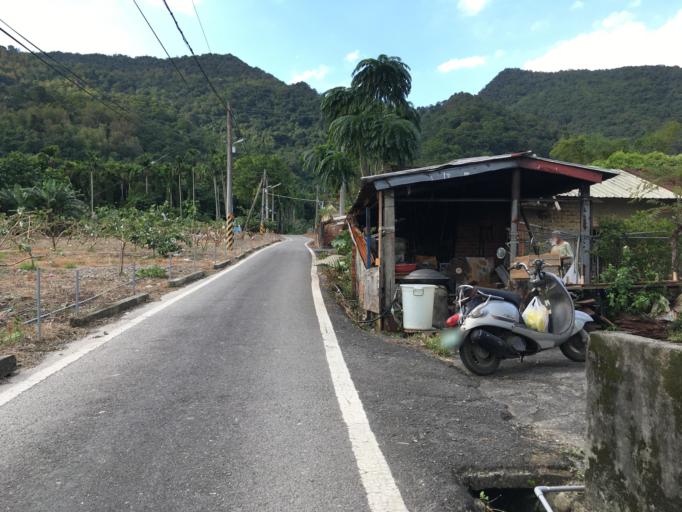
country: TW
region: Taiwan
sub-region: Yilan
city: Yilan
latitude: 24.8391
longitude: 121.7825
